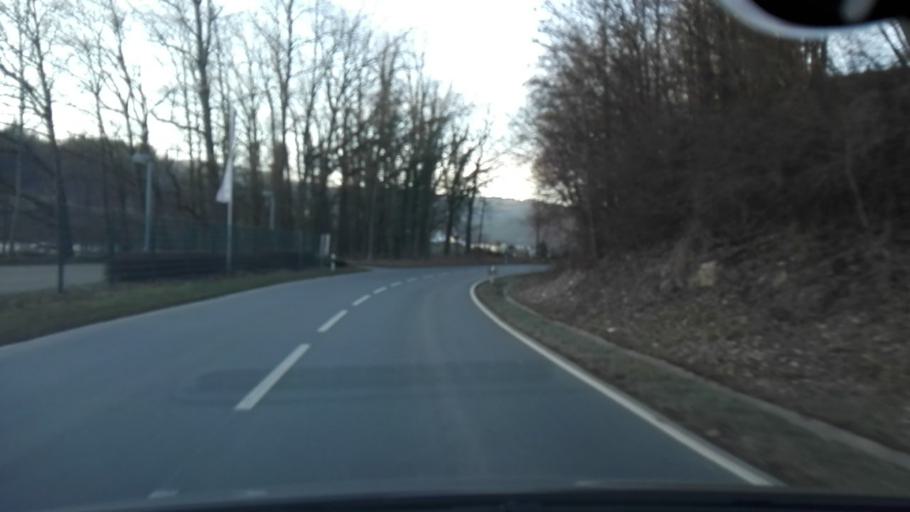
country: DE
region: North Rhine-Westphalia
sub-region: Regierungsbezirk Arnsberg
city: Finnentrop
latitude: 51.1962
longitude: 7.9742
